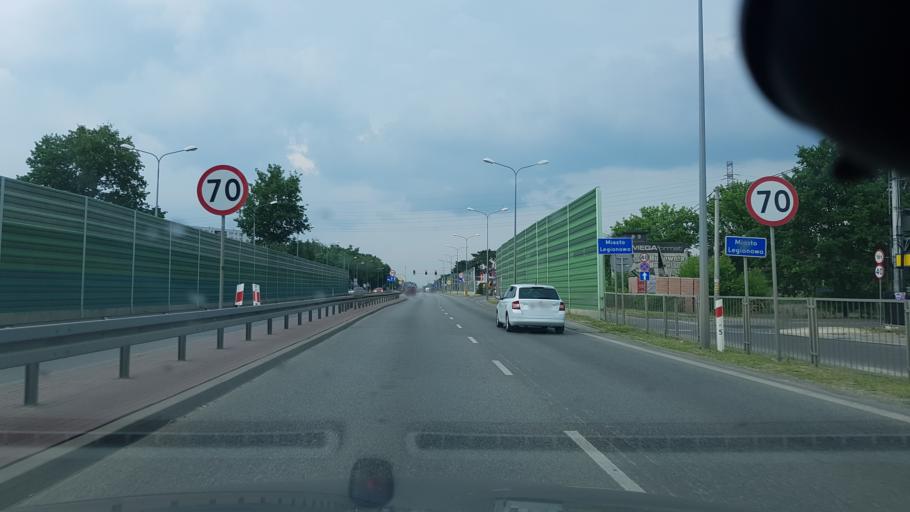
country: PL
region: Masovian Voivodeship
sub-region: Powiat legionowski
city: Jablonna
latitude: 52.3864
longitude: 20.9270
